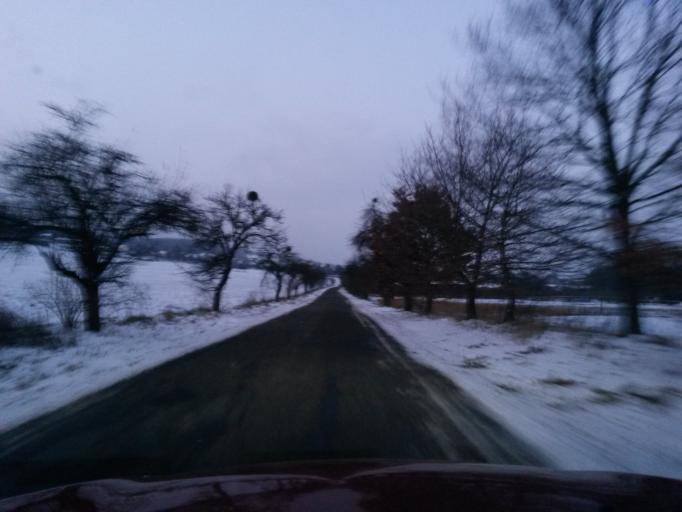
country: SK
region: Kosicky
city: Kosice
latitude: 48.7394
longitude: 21.3252
